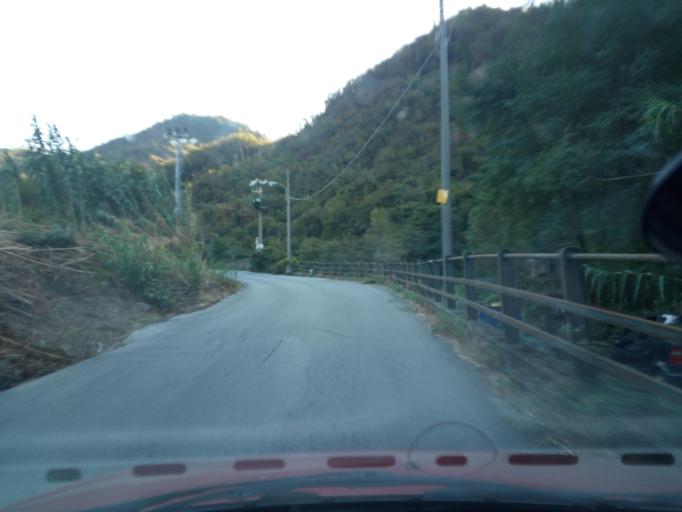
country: IT
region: Liguria
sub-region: Provincia di Genova
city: Isoverde
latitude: 44.4636
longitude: 8.8269
